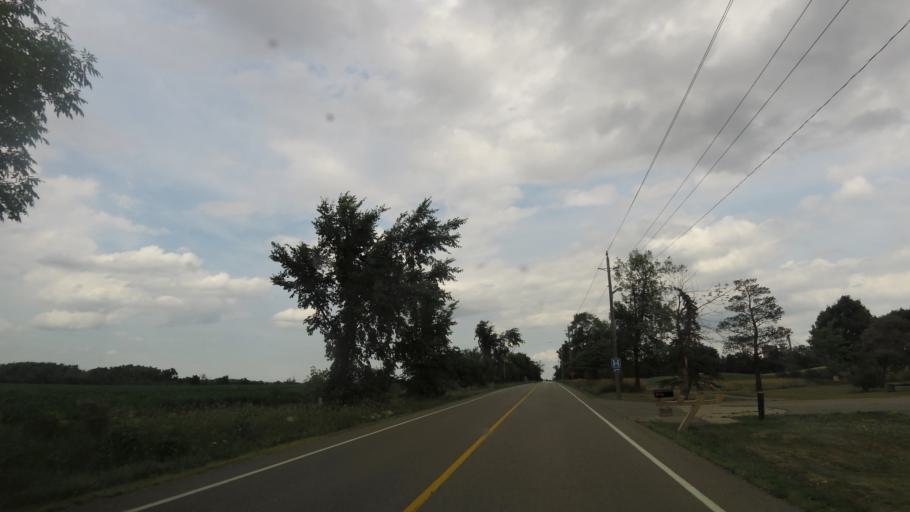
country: CA
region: Ontario
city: Brampton
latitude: 43.7897
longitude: -79.8115
